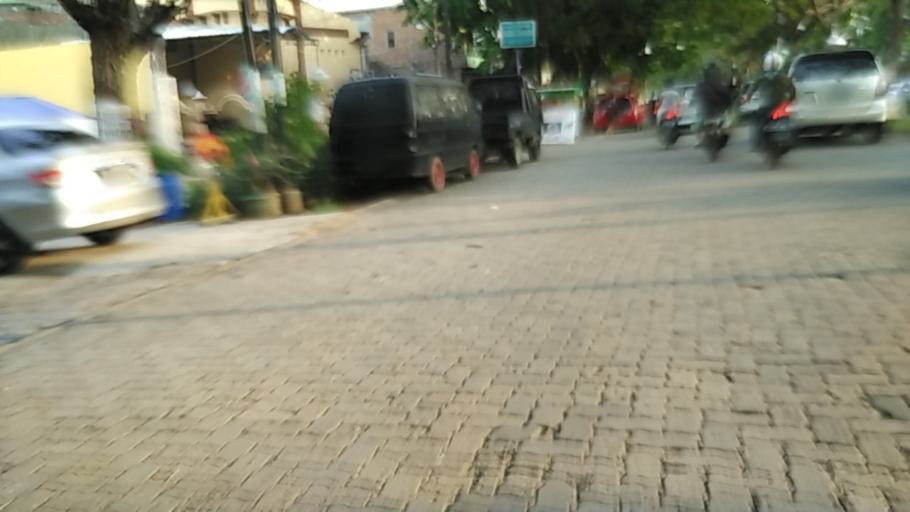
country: ID
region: Central Java
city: Semarang
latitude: -6.9720
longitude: 110.3906
